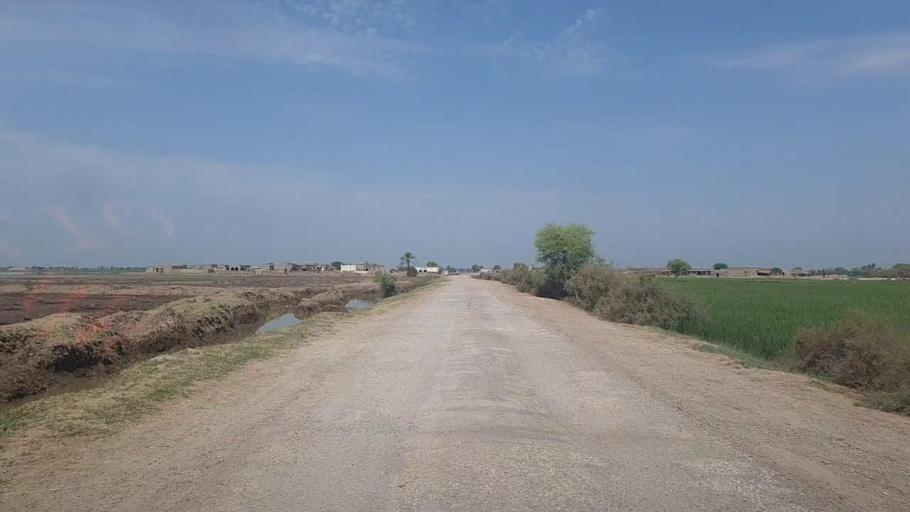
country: PK
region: Sindh
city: Thul
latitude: 28.2899
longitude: 68.6836
